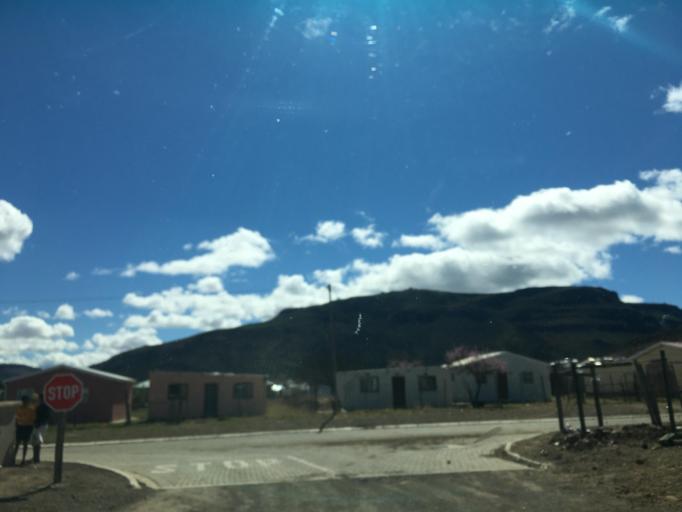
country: ZA
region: Eastern Cape
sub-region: Chris Hani District Municipality
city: Cala
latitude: -31.5385
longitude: 27.6991
